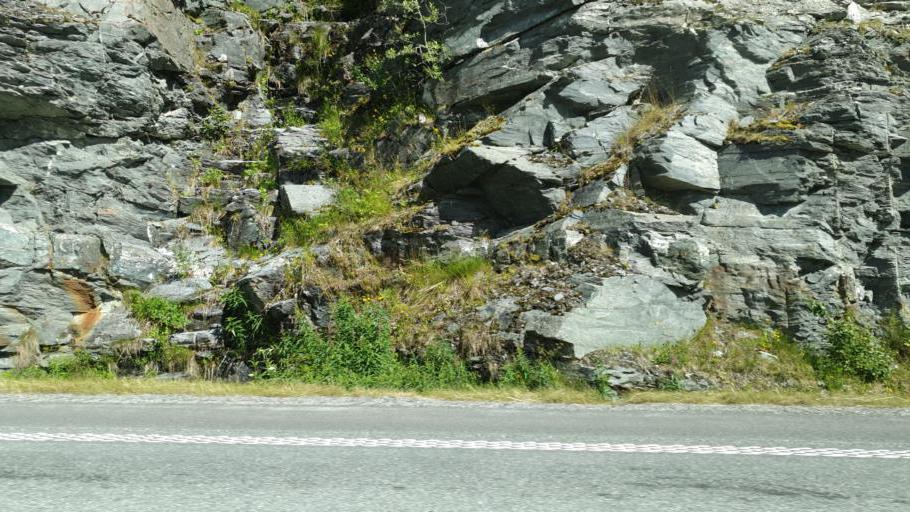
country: NO
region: Sor-Trondelag
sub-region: Oppdal
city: Oppdal
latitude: 62.4134
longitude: 9.6365
